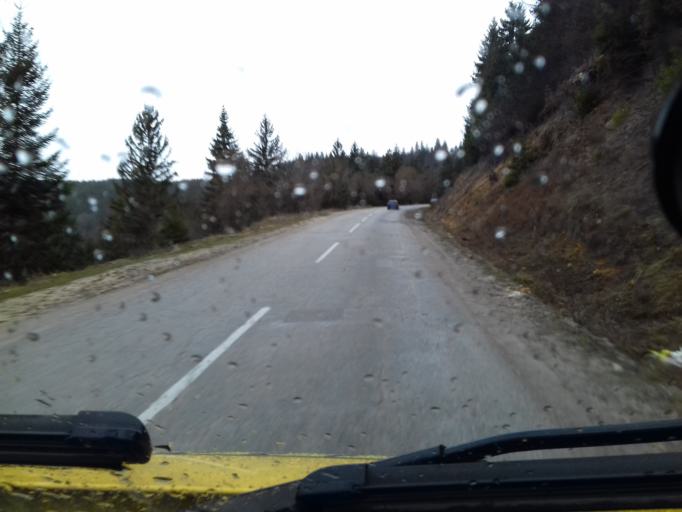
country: BA
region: Federation of Bosnia and Herzegovina
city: Turbe
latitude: 44.2796
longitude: 17.5091
